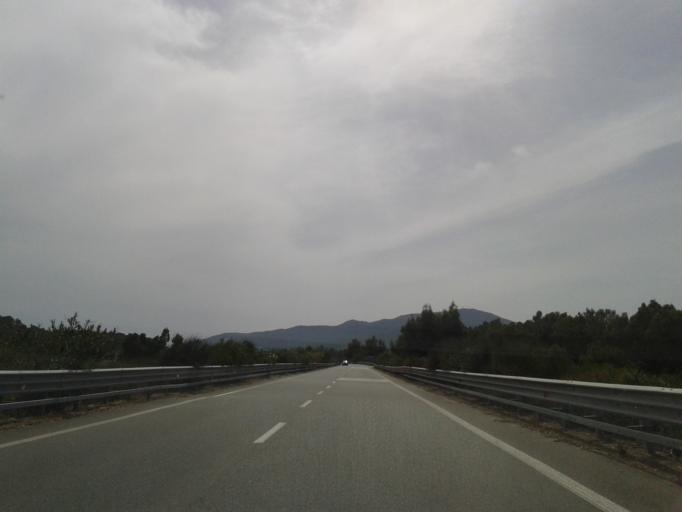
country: IT
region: Sardinia
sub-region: Provincia di Cagliari
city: Olia Speciosa
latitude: 39.2570
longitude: 9.5320
